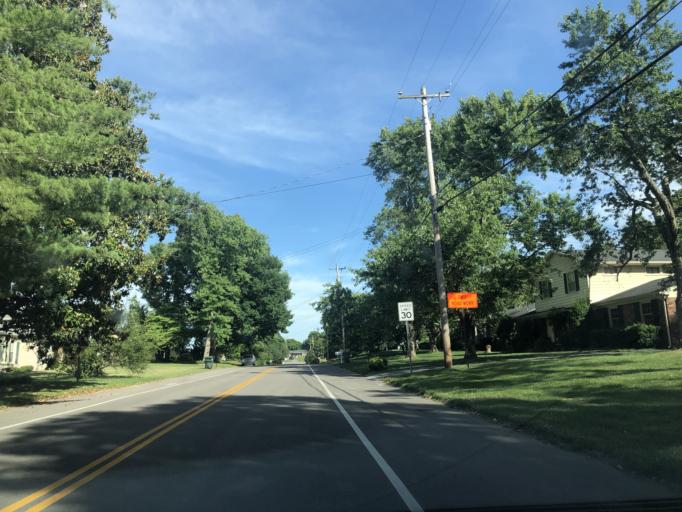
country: US
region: Tennessee
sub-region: Davidson County
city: Belle Meade
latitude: 36.0613
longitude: -86.9371
